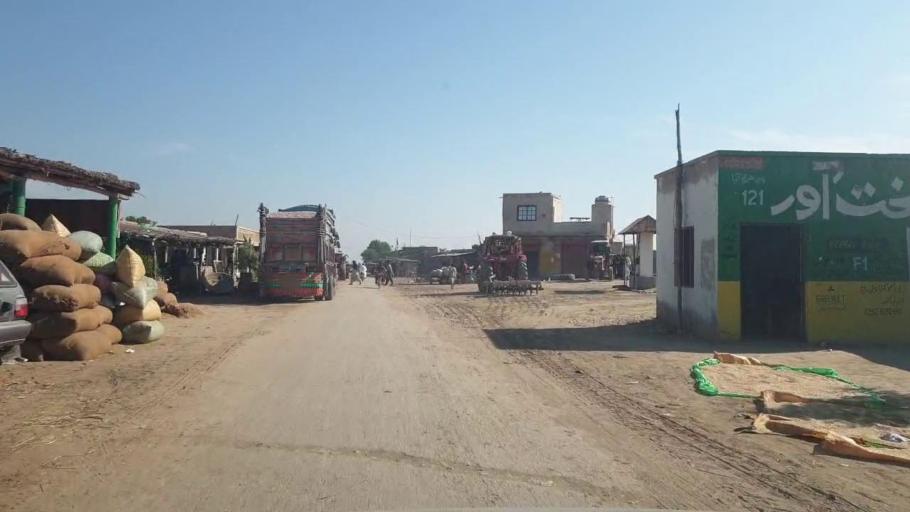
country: PK
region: Sindh
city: Rajo Khanani
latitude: 24.9211
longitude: 68.9287
